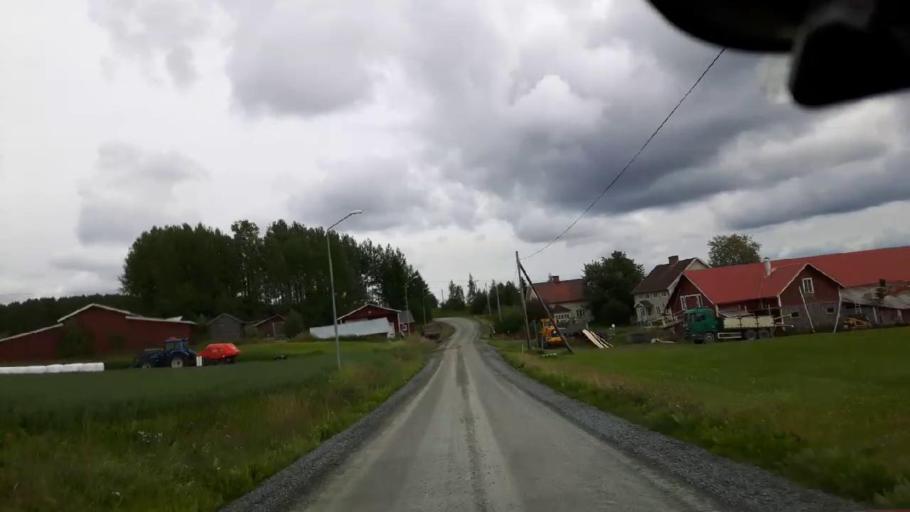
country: SE
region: Jaemtland
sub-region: Krokoms Kommun
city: Krokom
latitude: 63.5684
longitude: 14.2465
